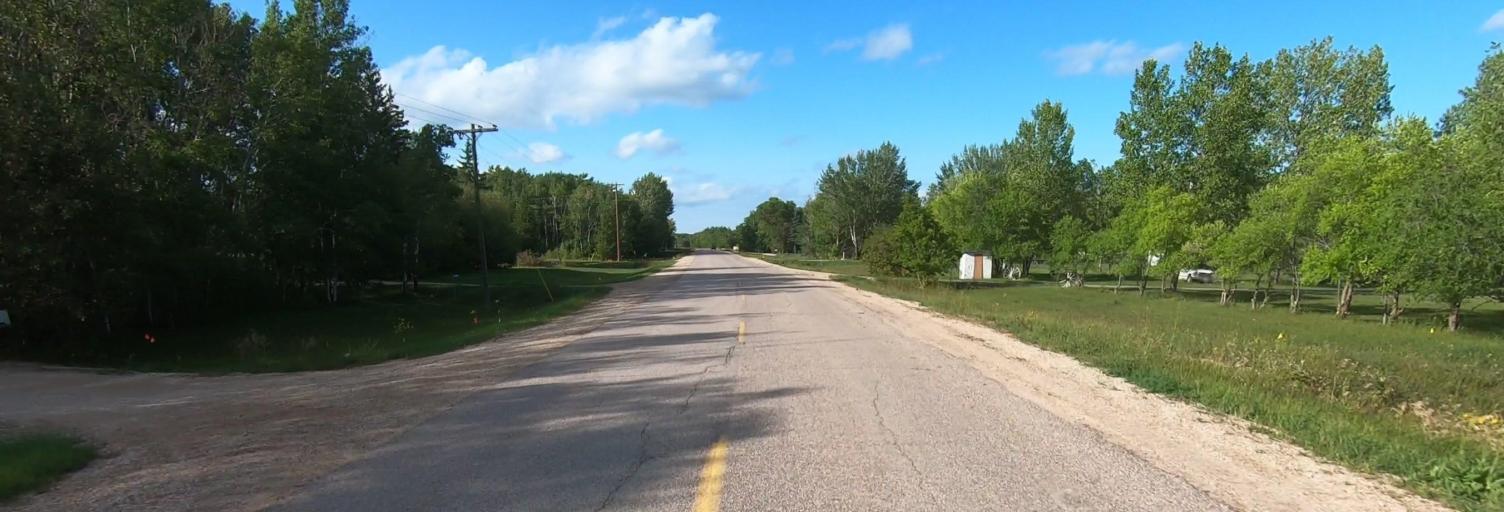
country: CA
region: Manitoba
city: Selkirk
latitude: 50.2180
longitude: -96.8392
